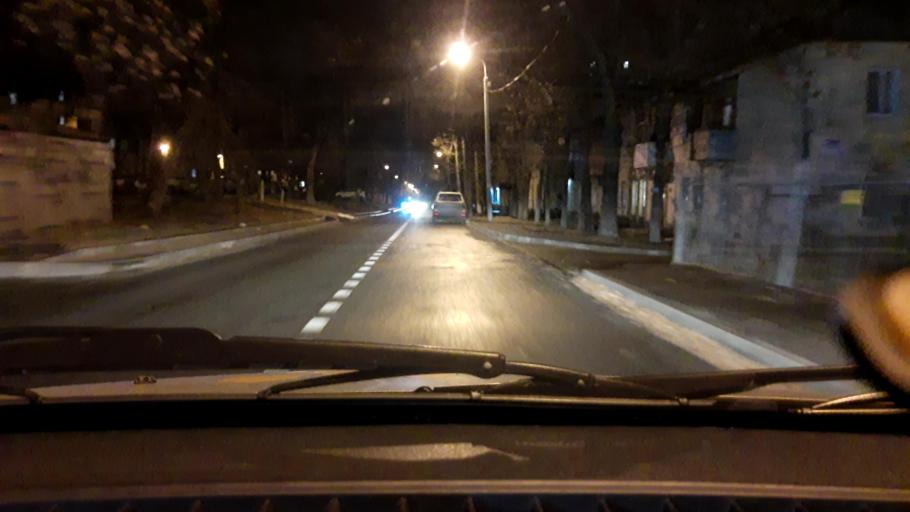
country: RU
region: Bashkortostan
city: Ufa
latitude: 54.7859
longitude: 56.0364
